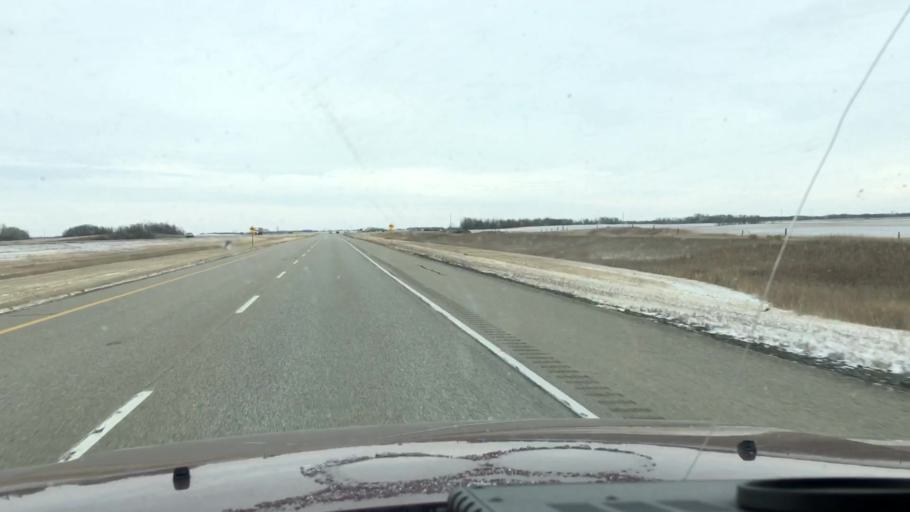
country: CA
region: Saskatchewan
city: Watrous
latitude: 51.3378
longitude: -106.0922
